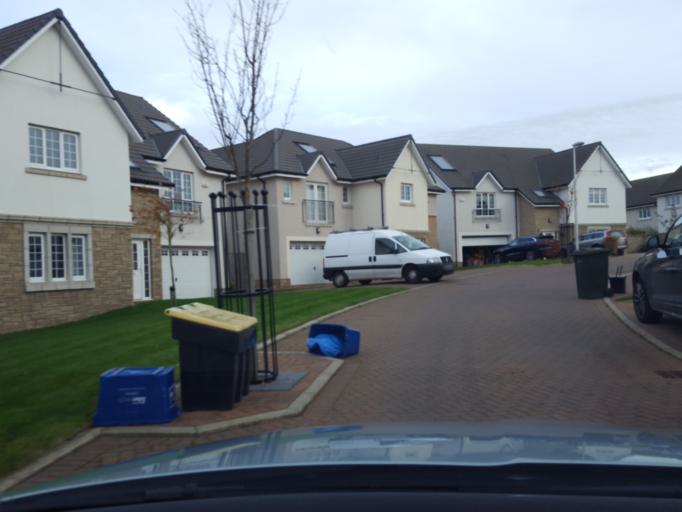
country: GB
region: Scotland
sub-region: Edinburgh
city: Ratho
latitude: 55.9252
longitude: -3.3726
